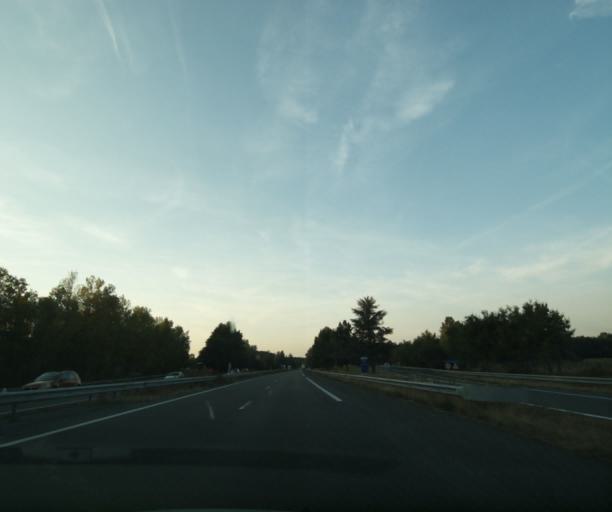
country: FR
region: Aquitaine
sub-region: Departement du Lot-et-Garonne
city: Damazan
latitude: 44.3412
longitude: 0.2519
